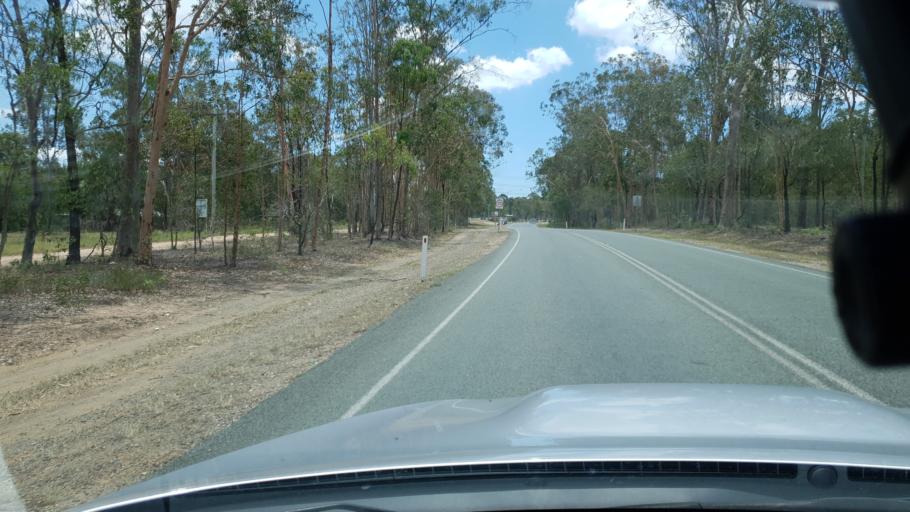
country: AU
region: Queensland
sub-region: Logan
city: North Maclean
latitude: -27.7332
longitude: 152.9849
